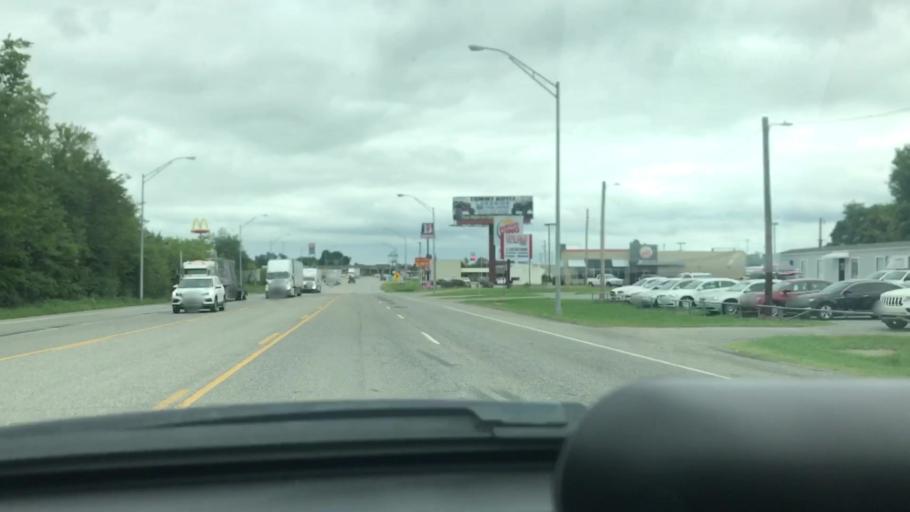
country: US
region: Oklahoma
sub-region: Wagoner County
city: Wagoner
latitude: 35.9547
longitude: -95.3952
